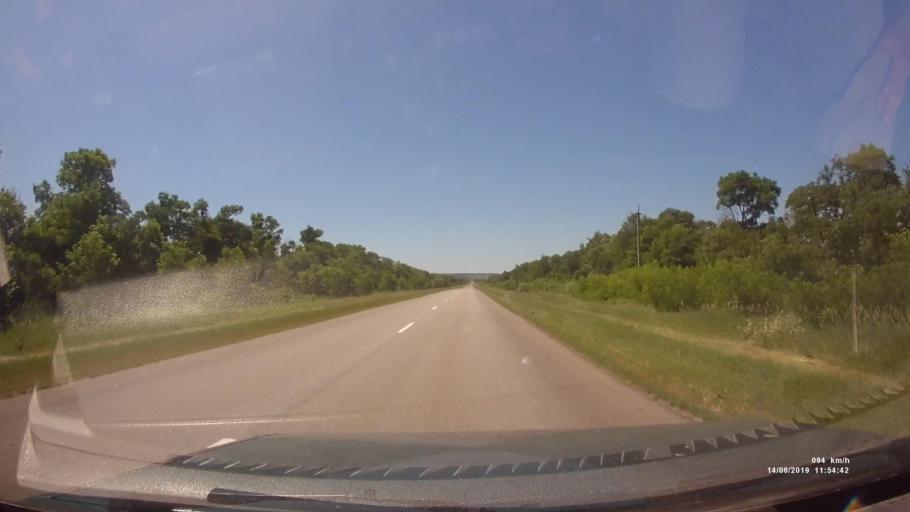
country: RU
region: Rostov
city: Kazanskaya
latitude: 49.8168
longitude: 41.1899
